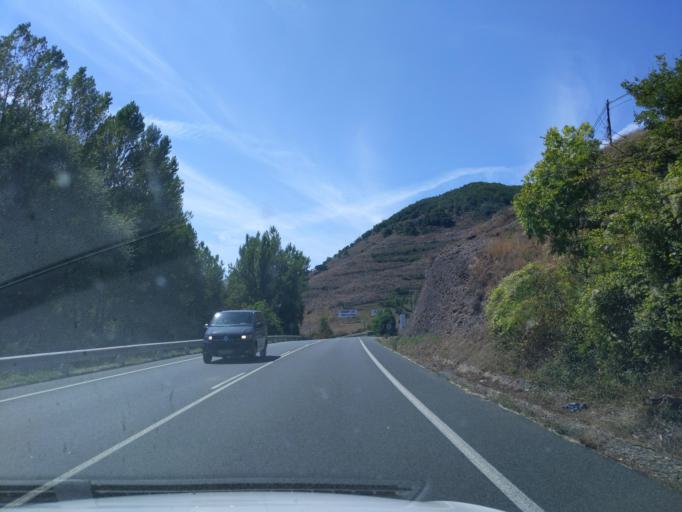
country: ES
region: La Rioja
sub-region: Provincia de La Rioja
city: Ojacastro
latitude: 42.3407
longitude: -3.0070
